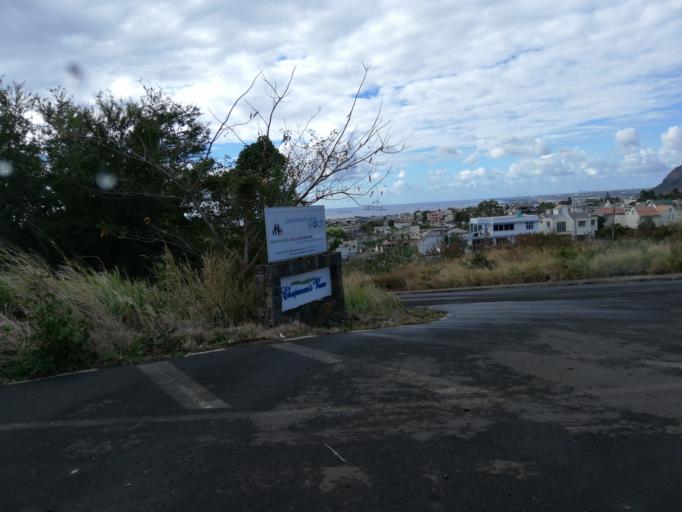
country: MU
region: Black River
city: Petite Riviere
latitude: -20.2042
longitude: 57.4637
